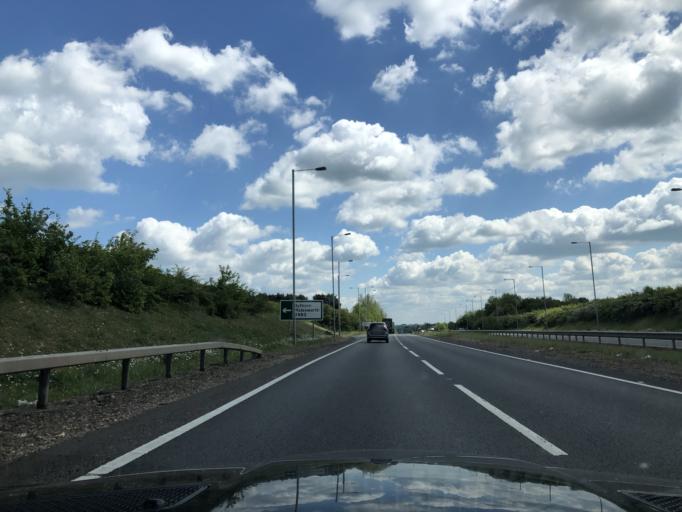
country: GB
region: England
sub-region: Northamptonshire
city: Raunds
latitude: 52.3737
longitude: -0.4627
